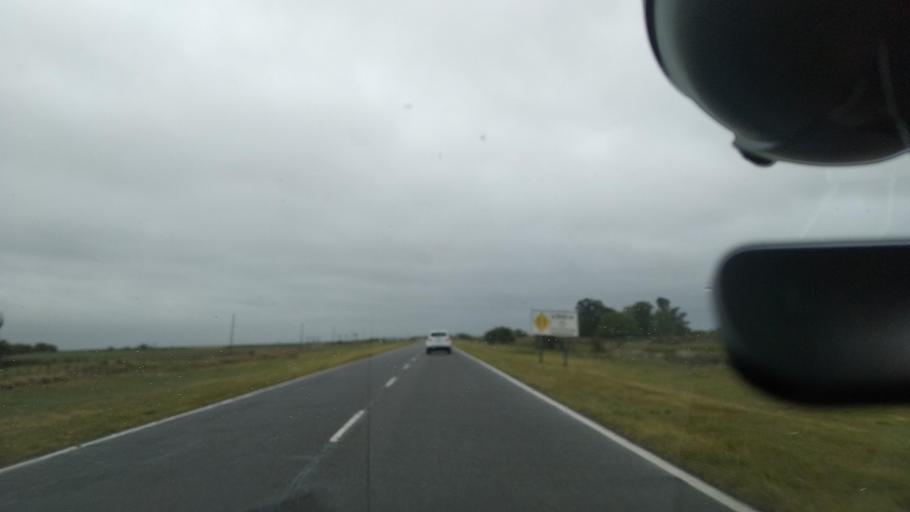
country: AR
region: Buenos Aires
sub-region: Partido de Dolores
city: Dolores
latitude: -36.1009
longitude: -57.4335
